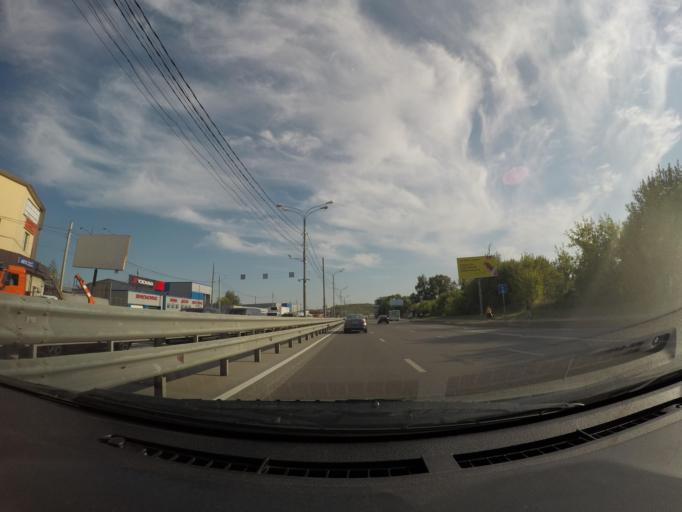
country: RU
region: Moskovskaya
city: Dolgoprudnyy
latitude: 55.9182
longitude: 37.4943
